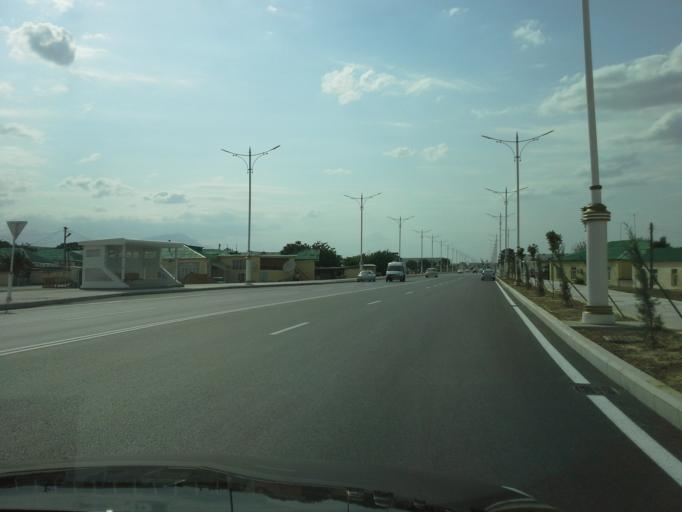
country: TM
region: Ahal
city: Ashgabat
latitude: 37.9587
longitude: 58.3393
